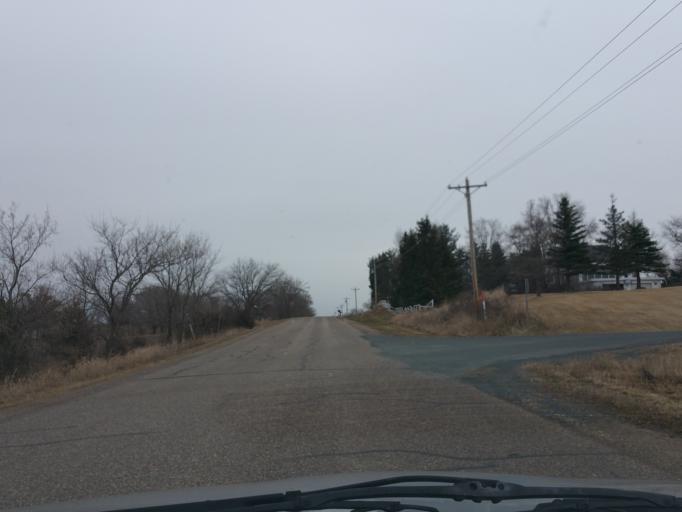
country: US
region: Wisconsin
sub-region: Saint Croix County
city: Roberts
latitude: 45.0034
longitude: -92.6424
